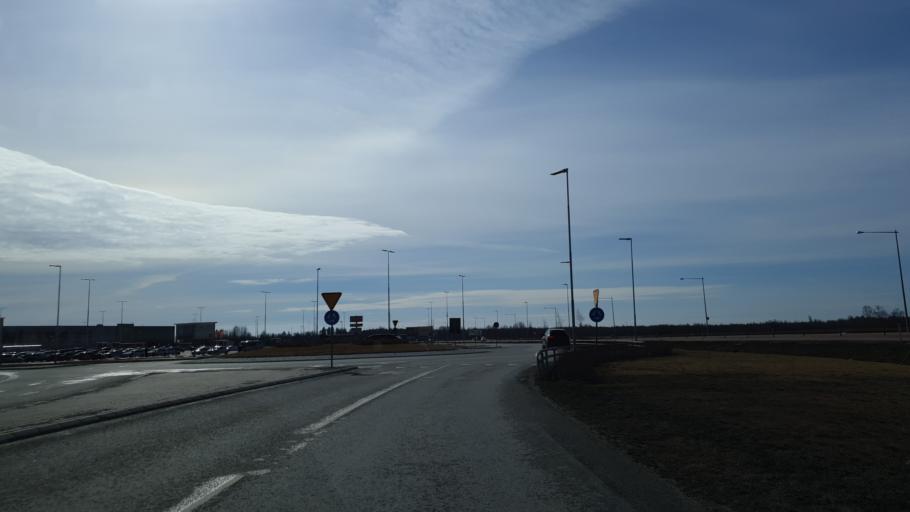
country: SE
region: Vaesterbotten
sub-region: Umea Kommun
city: Umea
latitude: 63.8075
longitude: 20.2501
